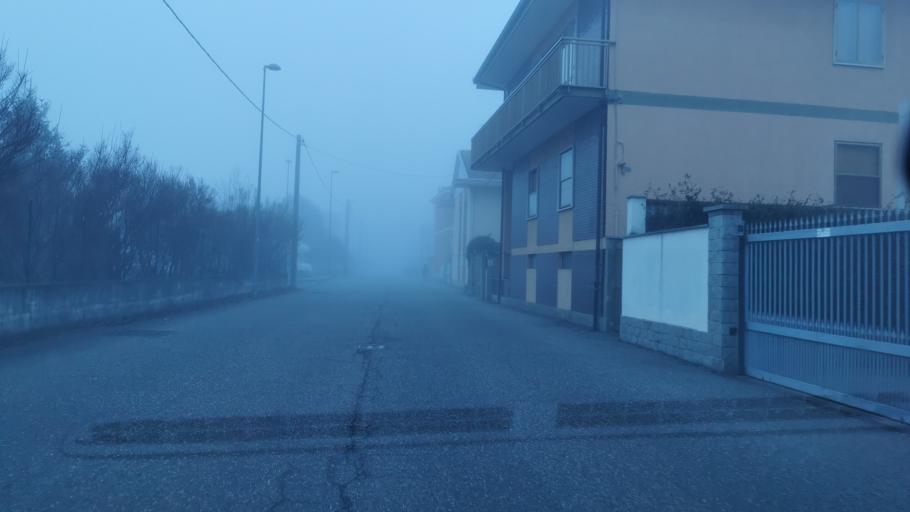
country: IT
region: Piedmont
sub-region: Provincia di Torino
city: Volpiano
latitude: 45.1966
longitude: 7.7673
